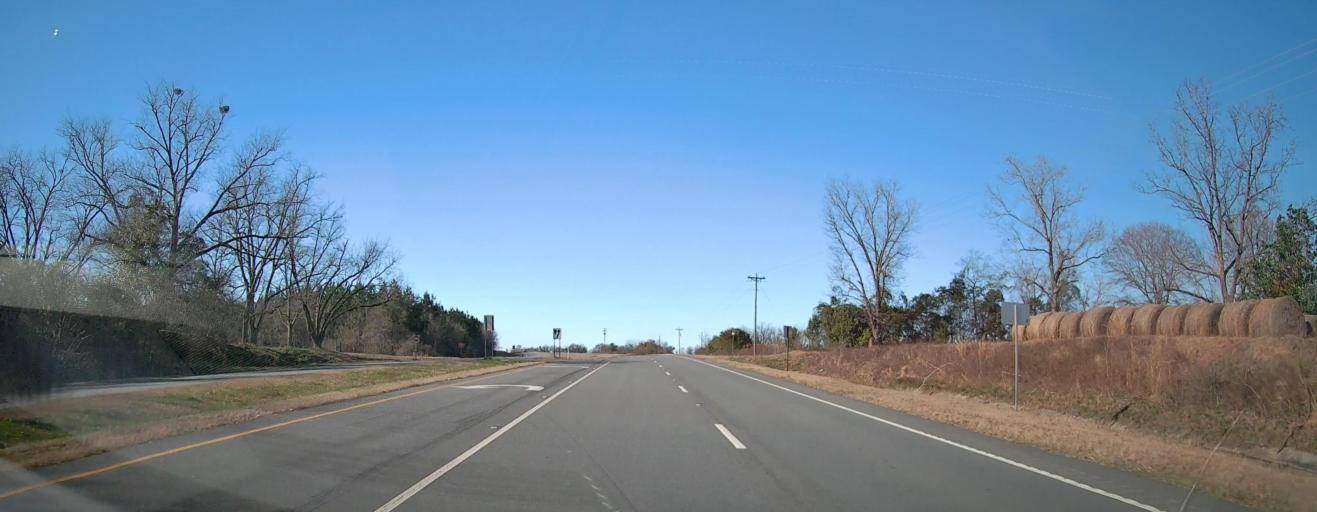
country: US
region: Georgia
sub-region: Taylor County
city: Butler
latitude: 32.6219
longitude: -84.2479
